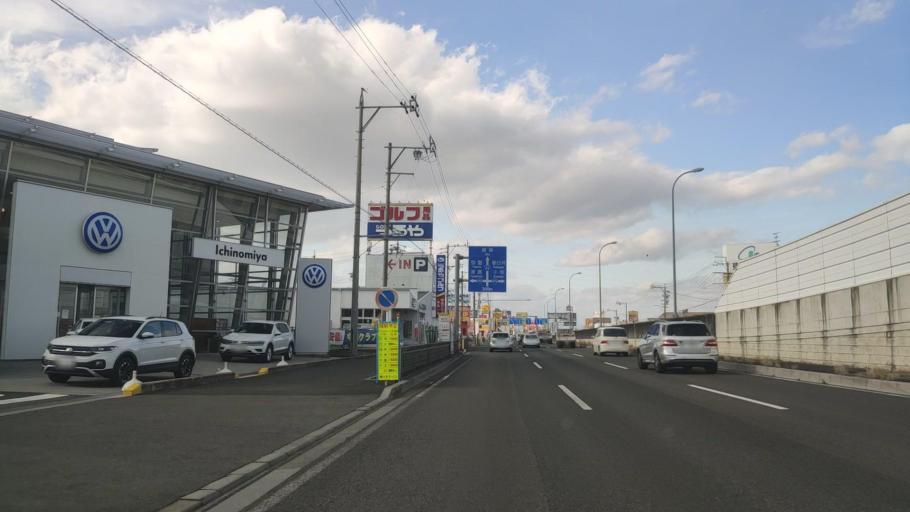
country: JP
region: Aichi
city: Ichinomiya
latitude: 35.2978
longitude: 136.8239
